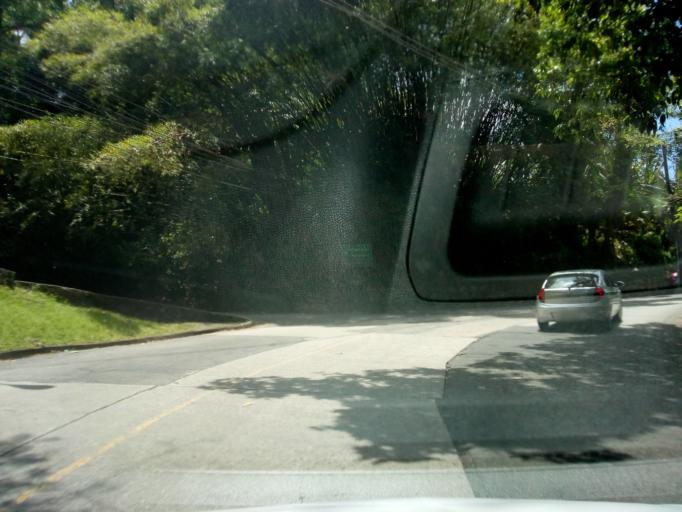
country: BR
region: Rio de Janeiro
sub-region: Rio De Janeiro
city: Rio de Janeiro
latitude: -22.9796
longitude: -43.2928
